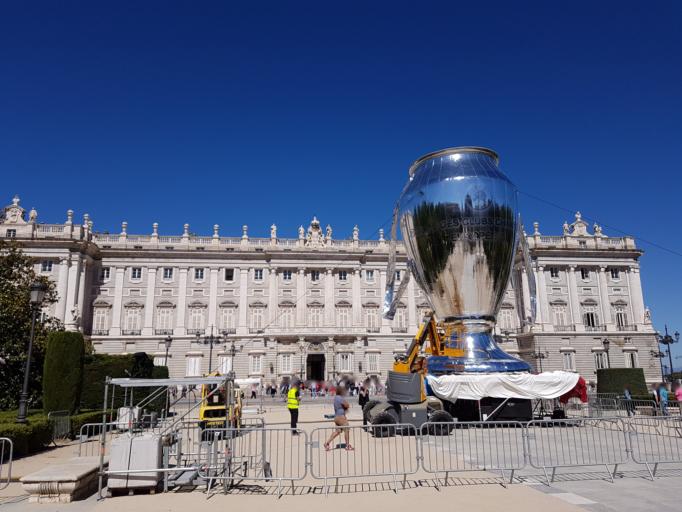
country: ES
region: Madrid
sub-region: Provincia de Madrid
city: City Center
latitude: 40.4183
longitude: -3.7123
